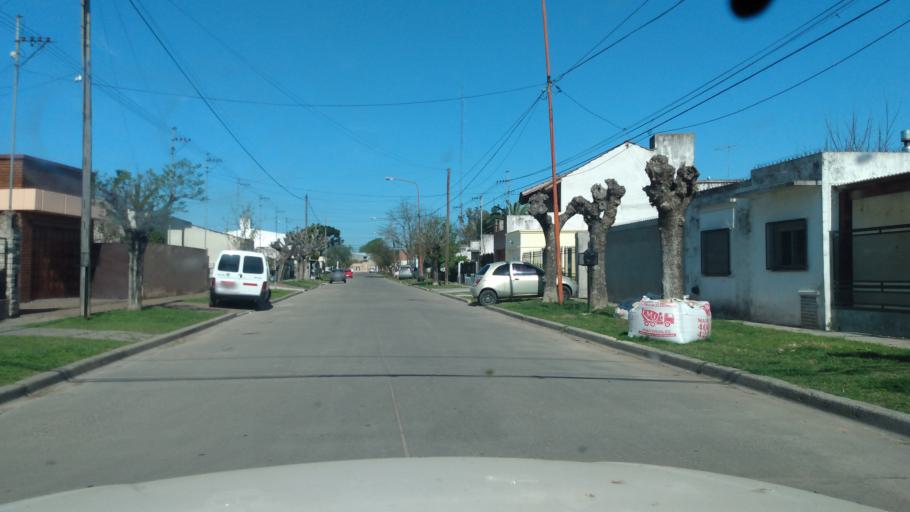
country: AR
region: Buenos Aires
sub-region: Partido de Lujan
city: Lujan
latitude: -34.5801
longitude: -59.1022
